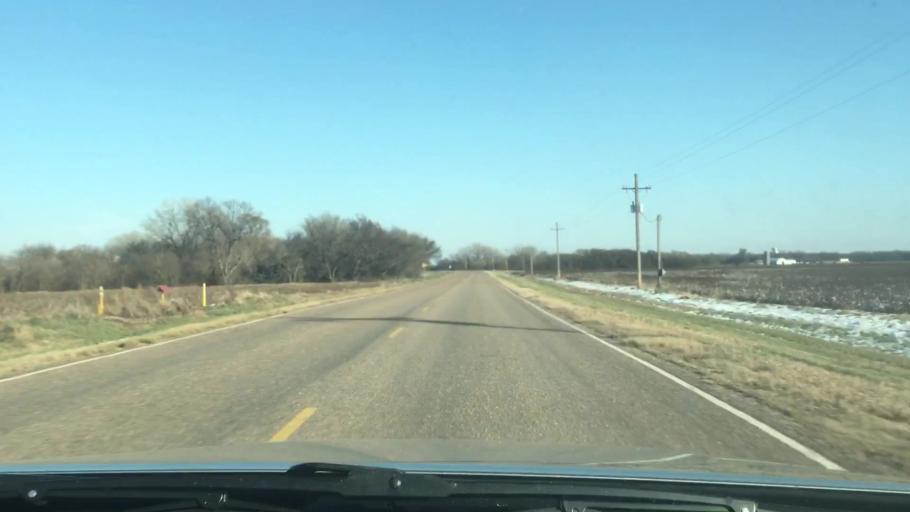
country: US
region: Kansas
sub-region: Rice County
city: Lyons
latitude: 38.2895
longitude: -98.1511
